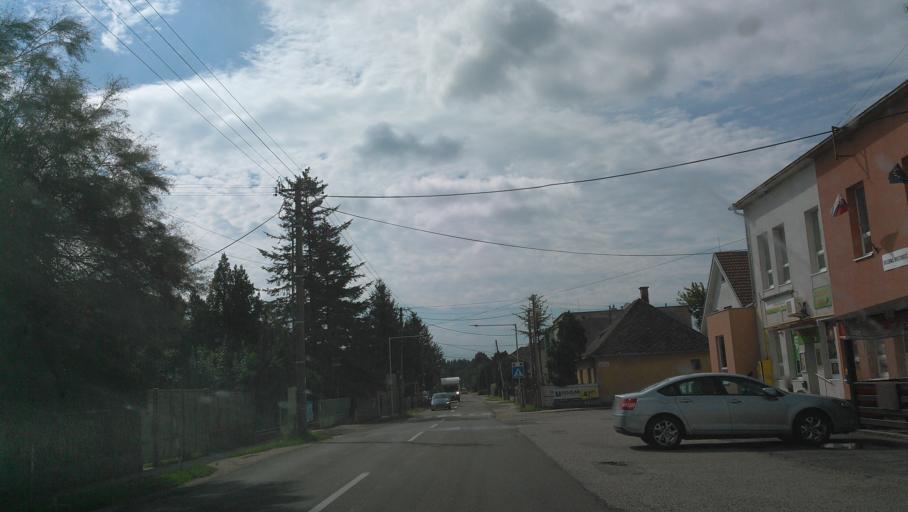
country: SK
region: Bratislavsky
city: Dunajska Luzna
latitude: 48.1689
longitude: 17.2763
